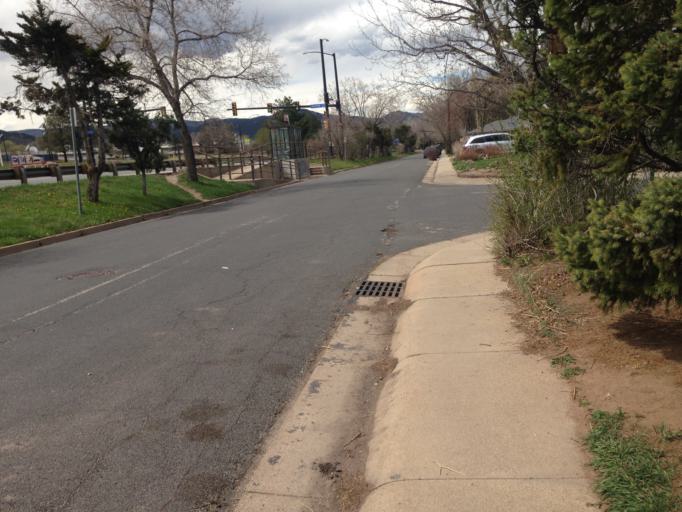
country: US
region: Colorado
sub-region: Boulder County
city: Boulder
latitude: 39.9933
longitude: -105.2585
